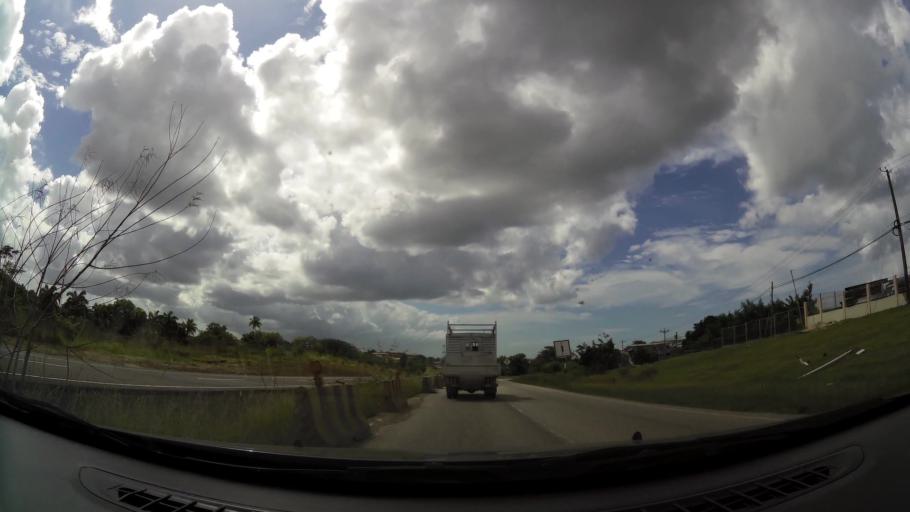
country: TT
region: City of San Fernando
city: San Fernando
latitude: 10.2475
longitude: -61.4935
